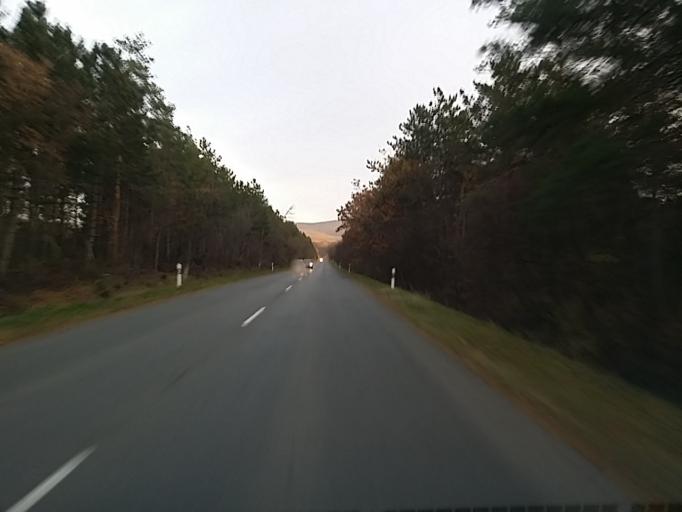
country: HU
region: Heves
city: Gyongyossolymos
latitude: 47.8189
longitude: 19.9615
